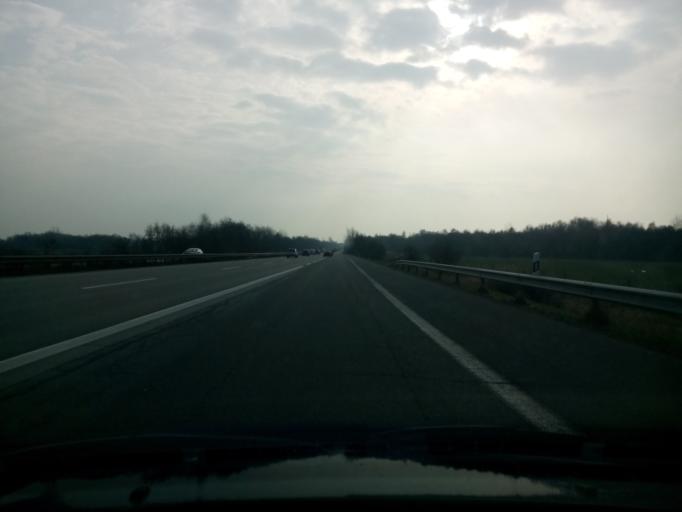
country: DE
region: Lower Saxony
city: Loxstedt
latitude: 53.4937
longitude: 8.6254
